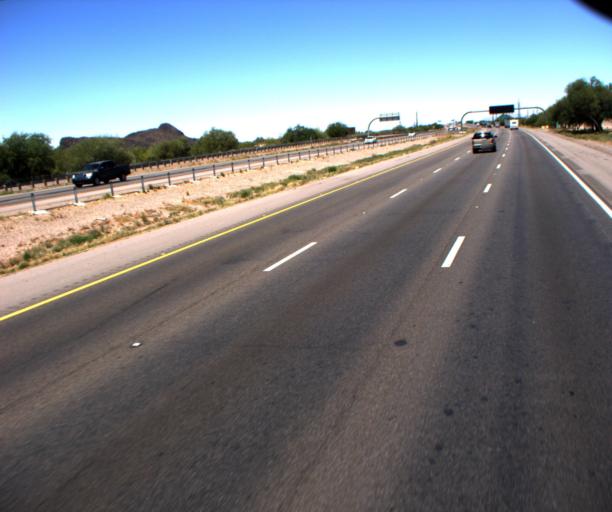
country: US
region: Arizona
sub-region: Pima County
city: Tortolita
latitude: 32.3893
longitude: -111.1177
